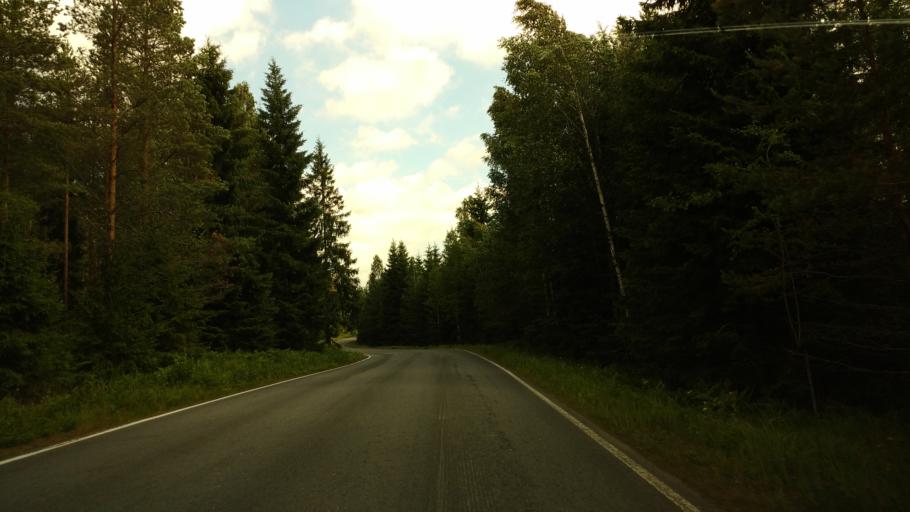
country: FI
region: Haeme
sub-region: Forssa
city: Ypaejae
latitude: 60.7421
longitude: 23.2012
